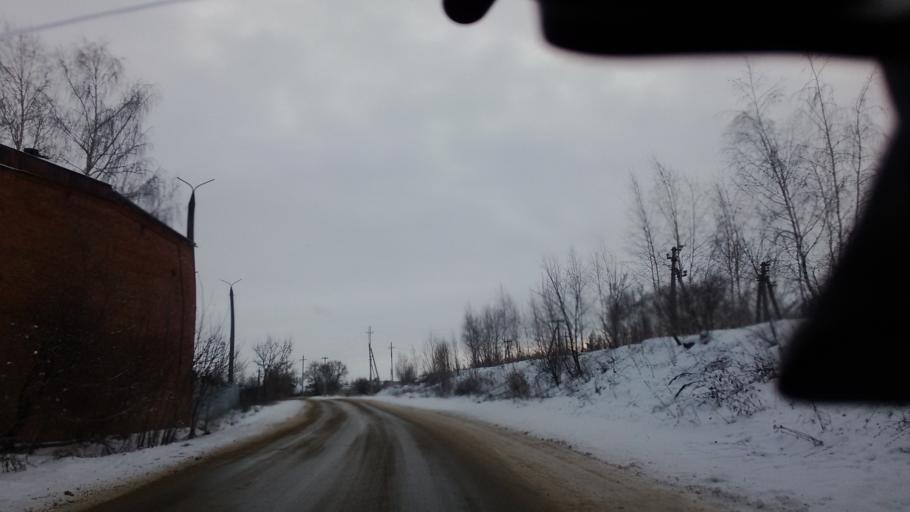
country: RU
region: Tula
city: Bogoroditsk
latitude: 53.7617
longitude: 38.1054
